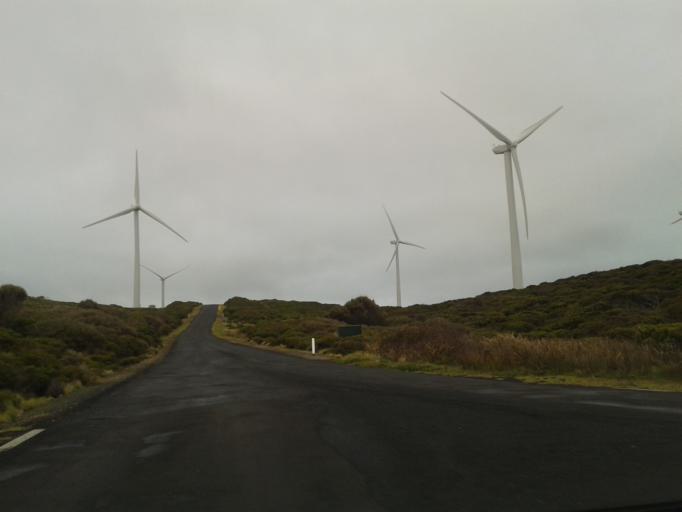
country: AU
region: Victoria
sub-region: Glenelg
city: Portland
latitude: -38.3792
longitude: 141.3696
